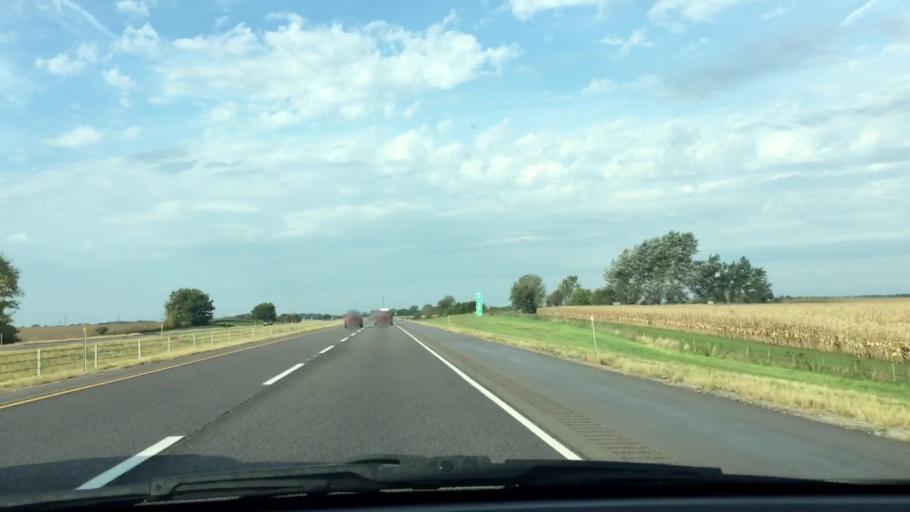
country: US
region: Illinois
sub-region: Lee County
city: Dixon
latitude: 41.7800
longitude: -89.5560
